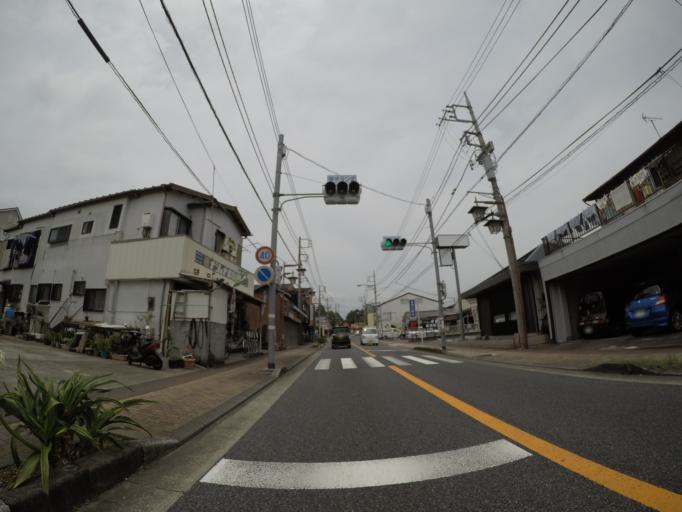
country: JP
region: Shizuoka
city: Fujinomiya
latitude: 35.2294
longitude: 138.6067
